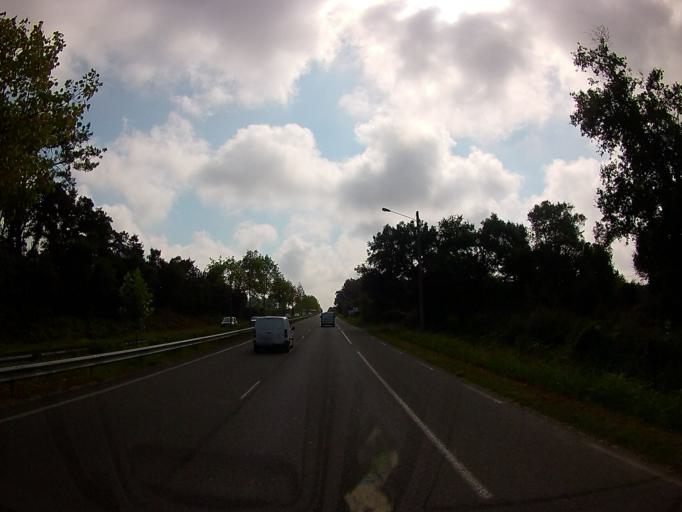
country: FR
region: Aquitaine
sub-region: Departement des Landes
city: Ondres
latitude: 43.5743
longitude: -1.4383
